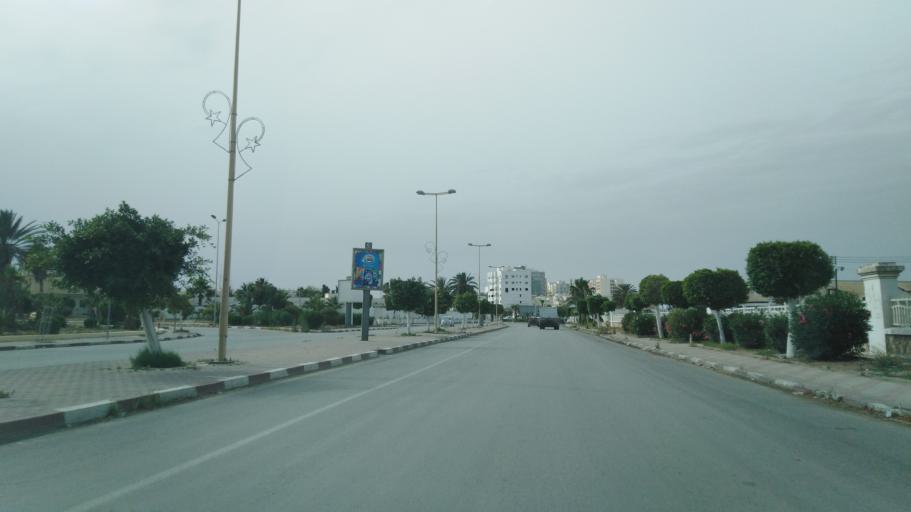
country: TN
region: Safaqis
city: Sfax
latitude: 34.7381
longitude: 10.7641
